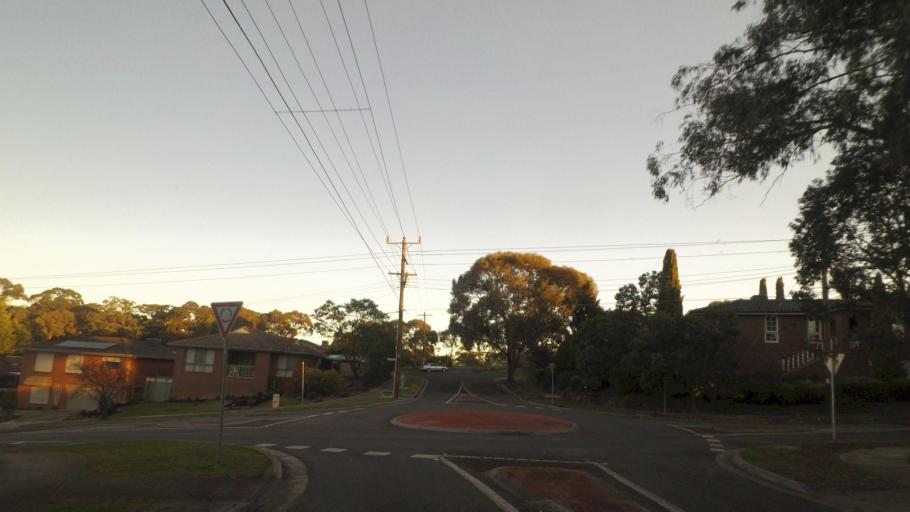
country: AU
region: Victoria
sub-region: Banyule
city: Watsonia North
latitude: -37.6906
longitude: 145.0915
